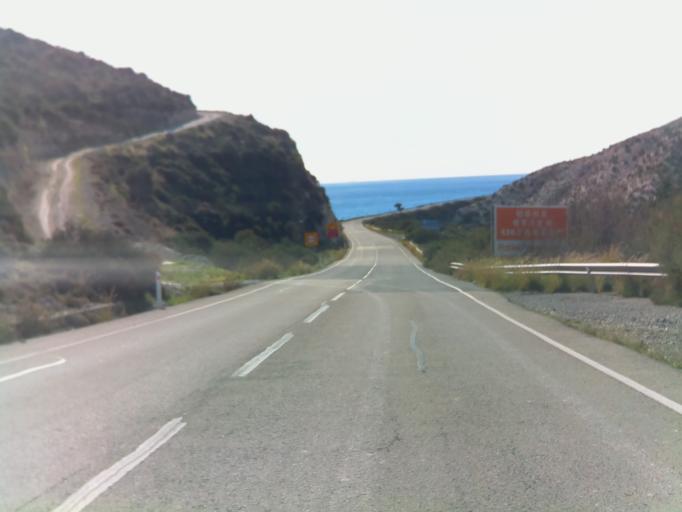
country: CY
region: Limassol
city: Pissouri
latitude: 34.6619
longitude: 32.6542
